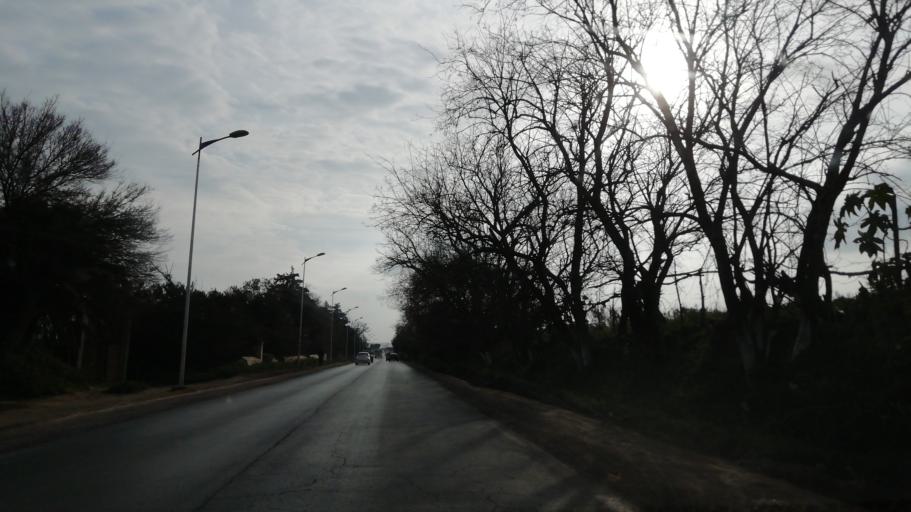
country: DZ
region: Mostaganem
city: Mostaganem
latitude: 35.8704
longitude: 0.0765
